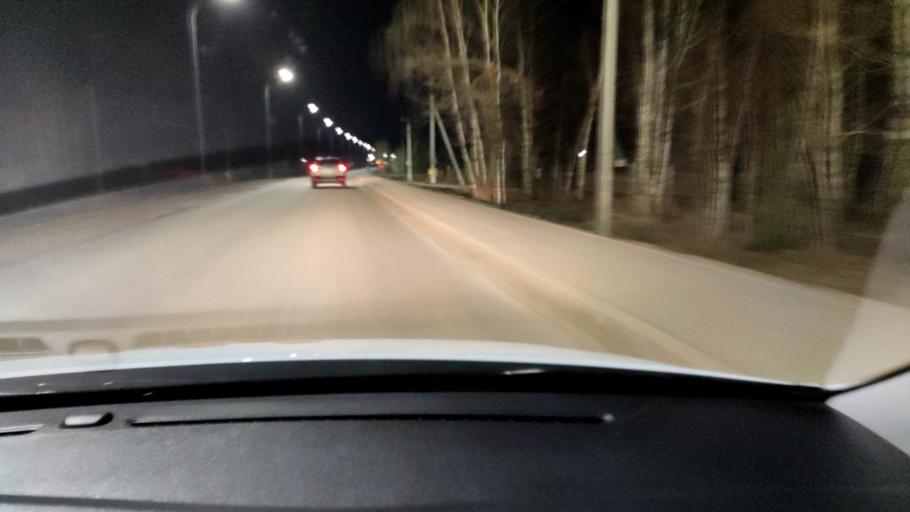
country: RU
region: Tatarstan
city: Stolbishchi
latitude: 55.6942
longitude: 49.2054
